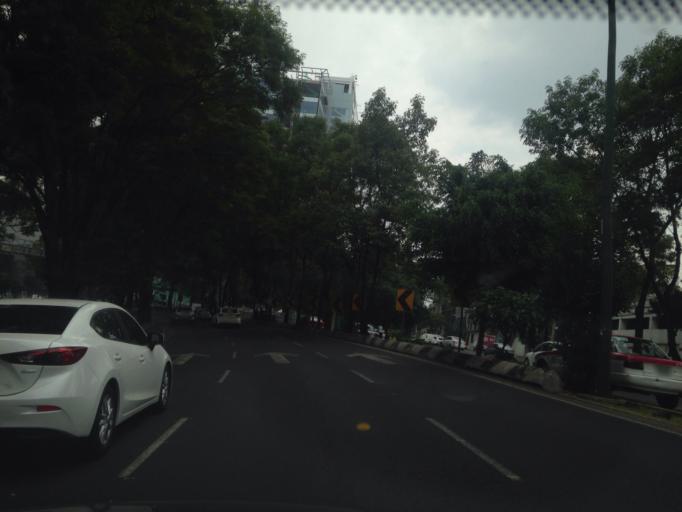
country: MX
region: Mexico City
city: Colonia del Valle
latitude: 19.3975
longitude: -99.1786
